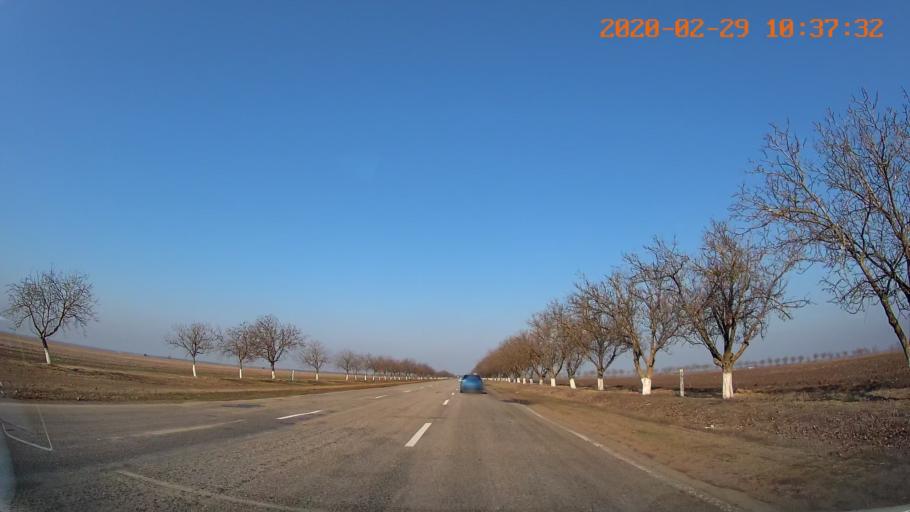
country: MD
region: Anenii Noi
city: Varnita
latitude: 47.0068
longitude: 29.4884
